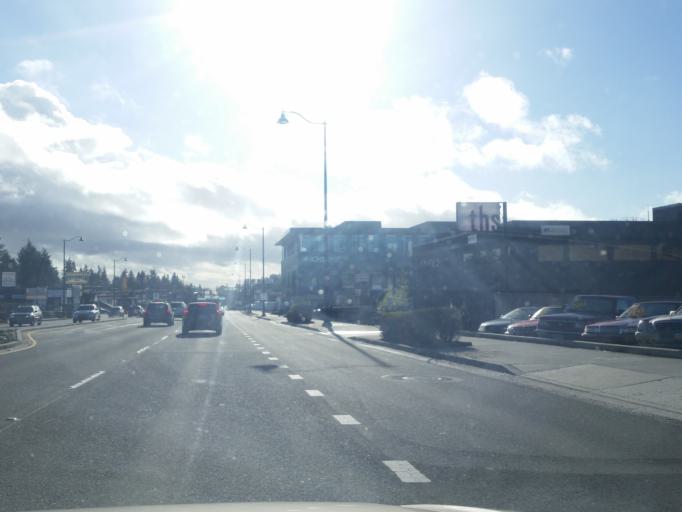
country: US
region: Washington
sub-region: King County
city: Shoreline
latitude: 47.7515
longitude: -122.3457
